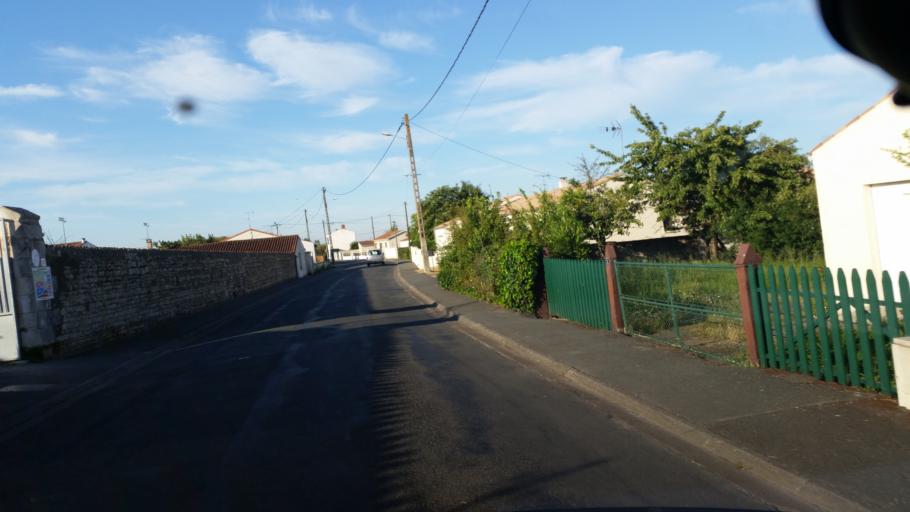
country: FR
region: Poitou-Charentes
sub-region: Departement de la Charente-Maritime
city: Marans
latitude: 46.3054
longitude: -0.9933
